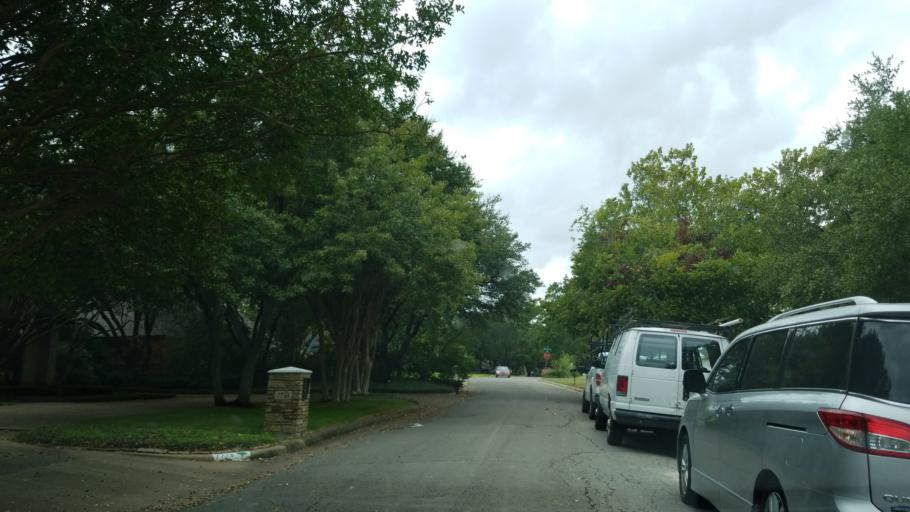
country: US
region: Texas
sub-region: Dallas County
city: Richardson
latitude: 32.9441
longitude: -96.7722
